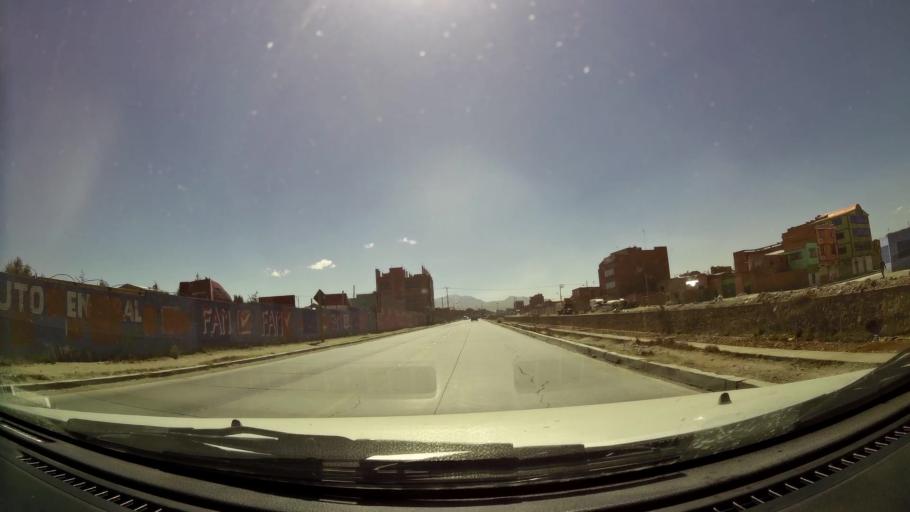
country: BO
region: La Paz
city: La Paz
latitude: -16.5007
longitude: -68.2089
